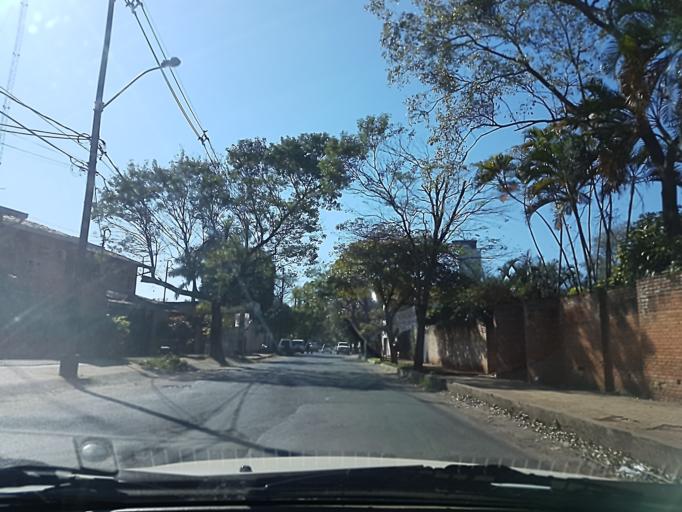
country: PY
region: Central
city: Lambare
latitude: -25.3012
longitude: -57.5779
